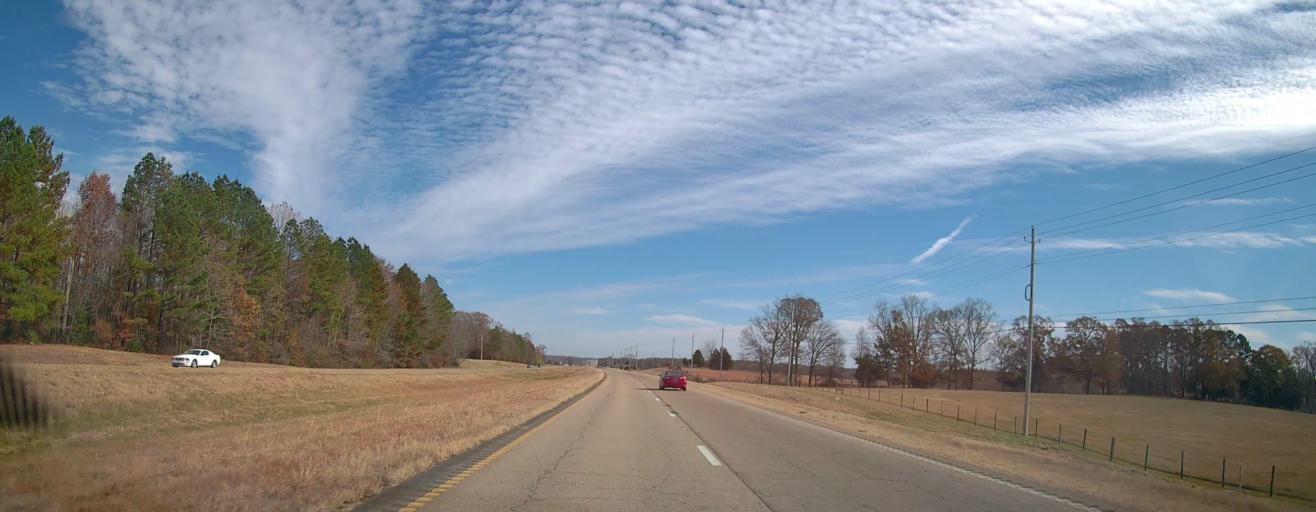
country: US
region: Mississippi
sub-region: Alcorn County
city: Corinth
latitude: 34.9310
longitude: -88.6369
